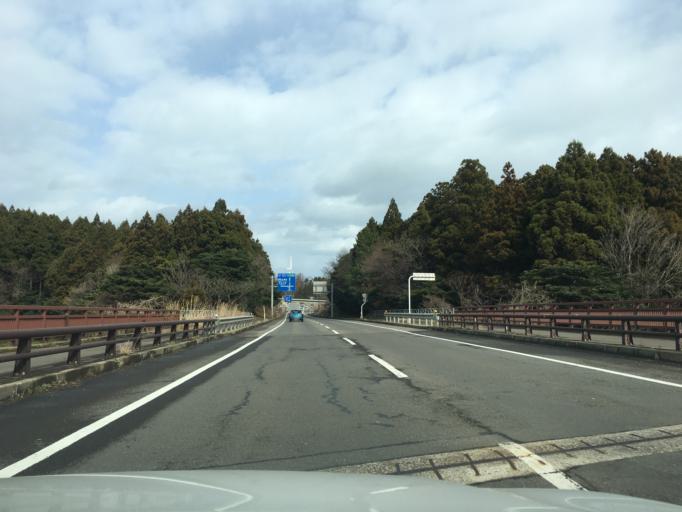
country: JP
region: Yamagata
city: Yuza
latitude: 39.2612
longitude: 139.9254
